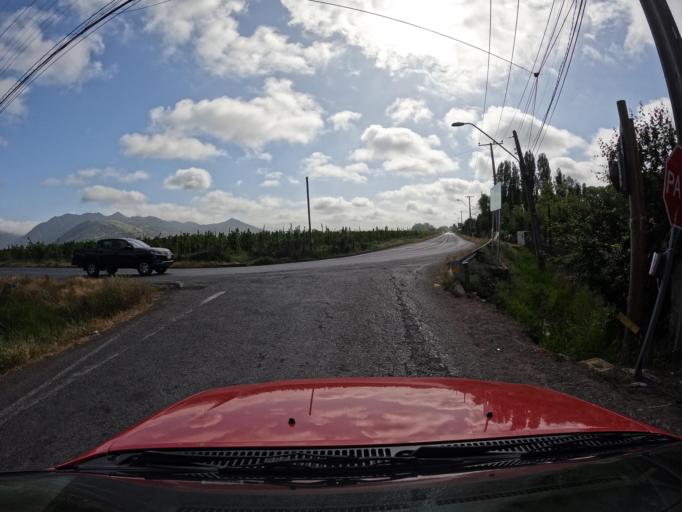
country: CL
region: Maule
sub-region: Provincia de Curico
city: Teno
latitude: -34.8729
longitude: -71.2254
